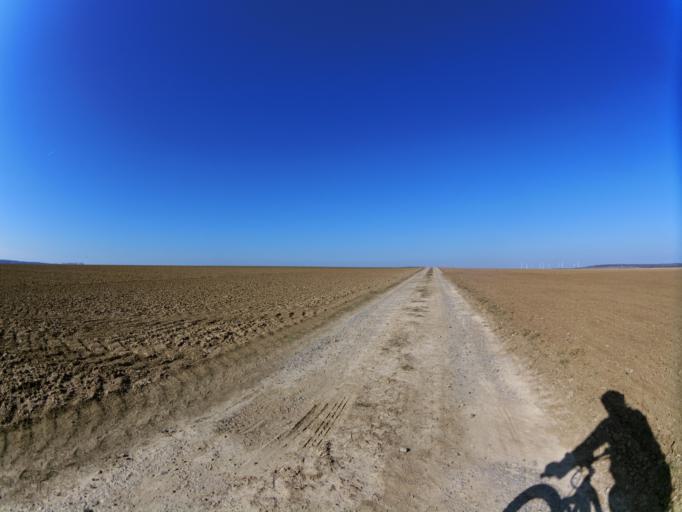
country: DE
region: Bavaria
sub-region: Regierungsbezirk Unterfranken
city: Unterpleichfeld
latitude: 49.8776
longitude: 10.0593
